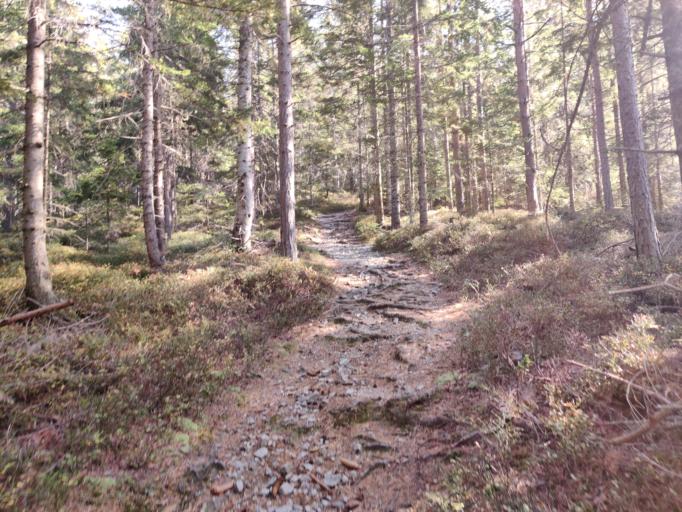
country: AT
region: Styria
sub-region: Politischer Bezirk Hartberg-Fuerstenfeld
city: Sankt Jakob im Walde
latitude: 47.4695
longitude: 15.8148
